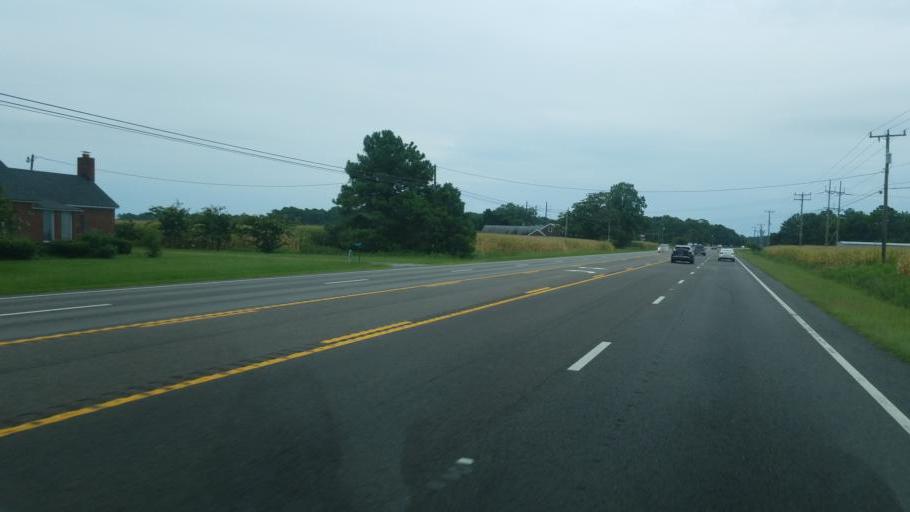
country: US
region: North Carolina
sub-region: Dare County
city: Southern Shores
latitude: 36.1907
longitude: -75.8640
